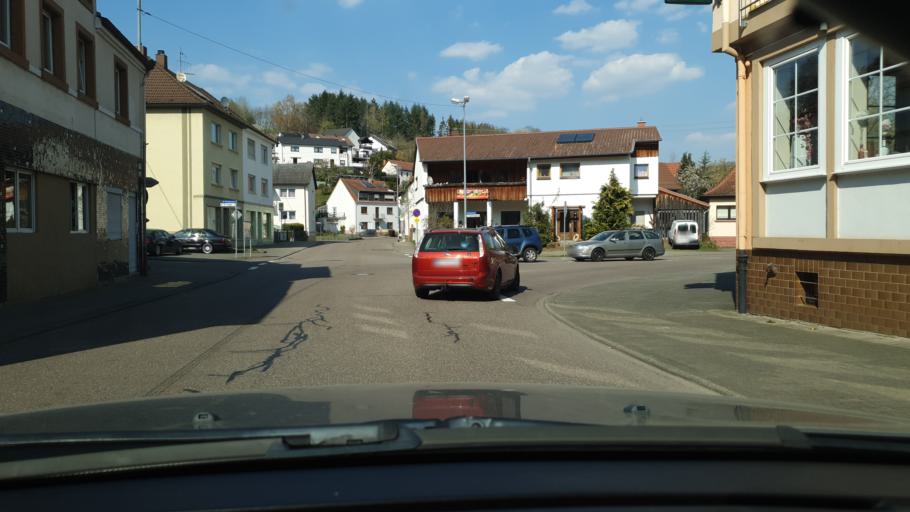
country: DE
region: Rheinland-Pfalz
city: Grossbundenbach
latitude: 49.2764
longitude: 7.4214
